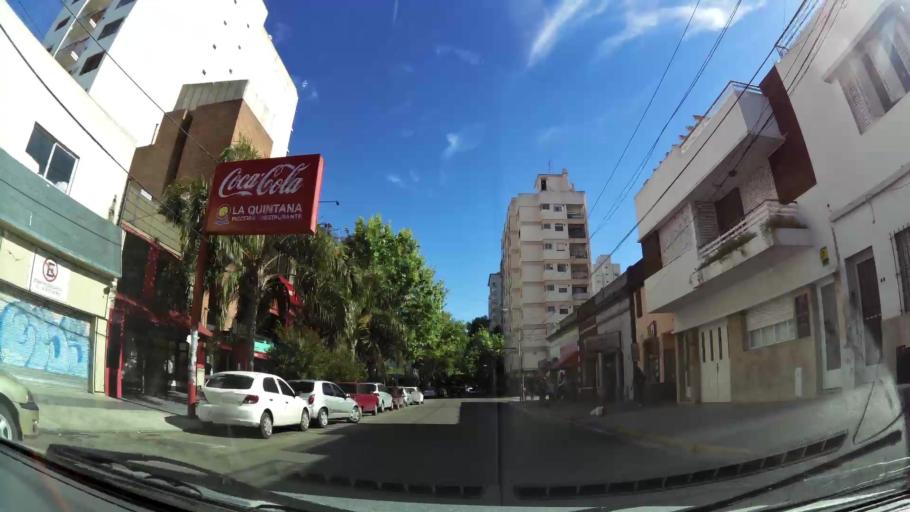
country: AR
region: Buenos Aires
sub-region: Partido de Lomas de Zamora
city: Lomas de Zamora
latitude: -34.7599
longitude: -58.4040
